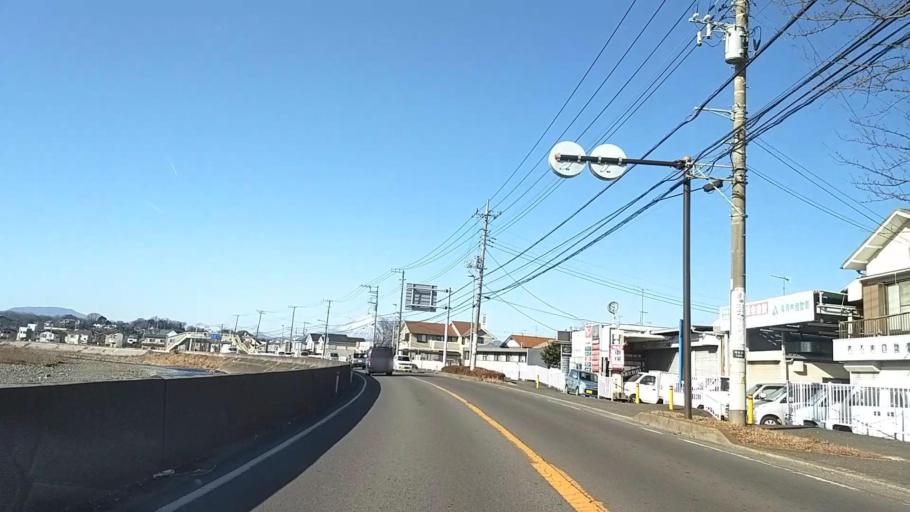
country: JP
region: Kanagawa
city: Isehara
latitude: 35.3597
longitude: 139.2961
